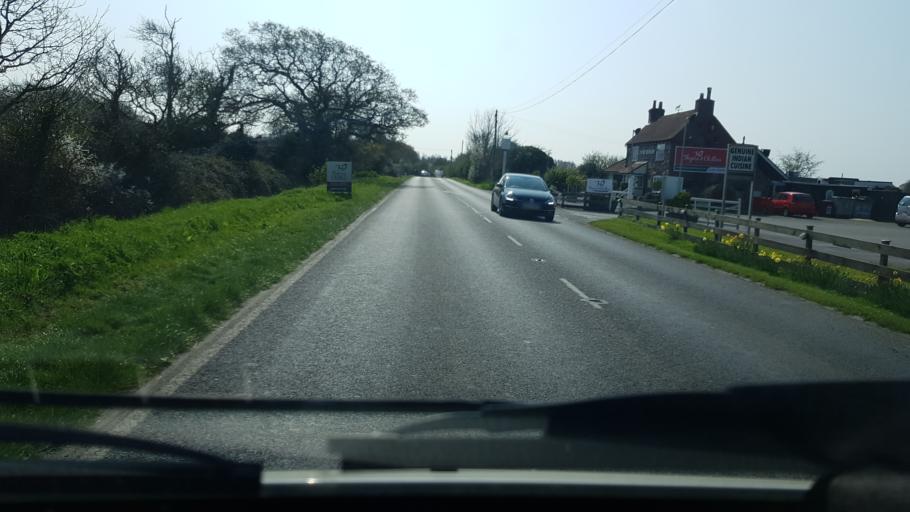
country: GB
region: England
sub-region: West Sussex
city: Birdham
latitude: 50.8128
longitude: -0.8032
